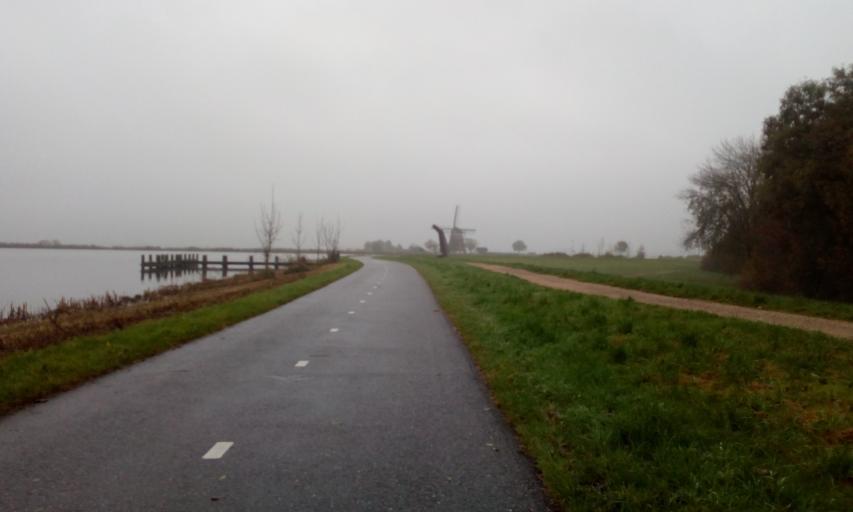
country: NL
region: South Holland
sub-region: Gemeente Lansingerland
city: Bleiswijk
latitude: 52.0058
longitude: 4.5515
